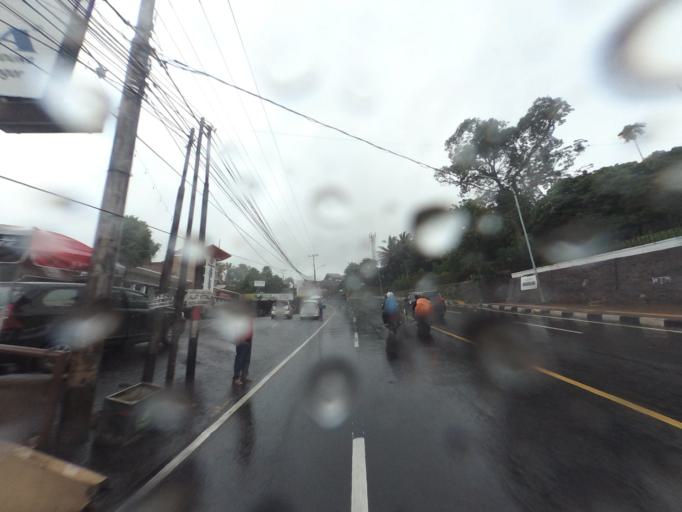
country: ID
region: West Java
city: Caringin
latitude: -6.6540
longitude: 106.8741
